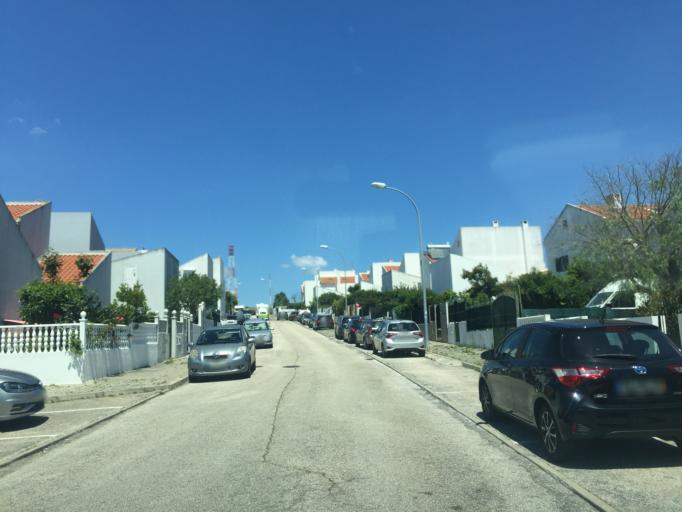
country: PT
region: Lisbon
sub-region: Oeiras
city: Quejas
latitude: 38.7232
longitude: -9.2673
